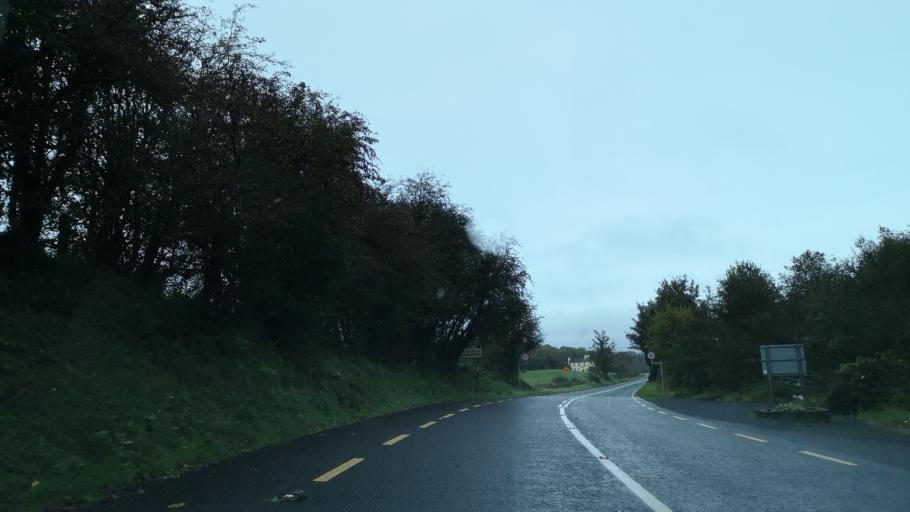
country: IE
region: Connaught
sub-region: Maigh Eo
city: Ballyhaunis
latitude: 53.7673
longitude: -8.7646
